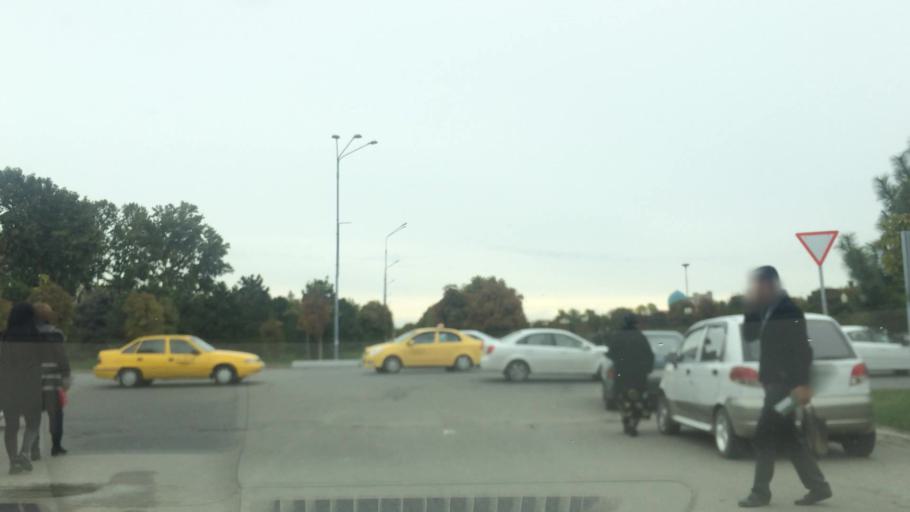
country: UZ
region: Samarqand
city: Samarqand
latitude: 39.6533
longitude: 66.9777
